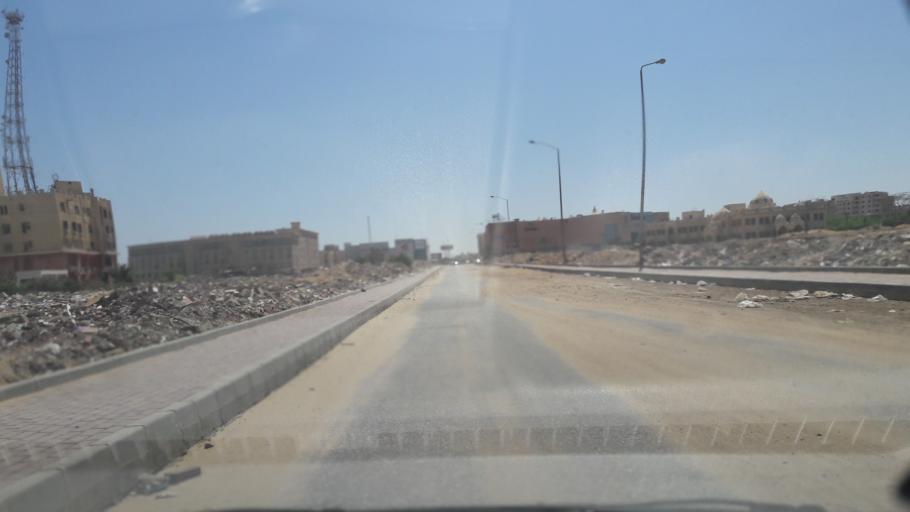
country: EG
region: Al Jizah
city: Madinat Sittah Uktubar
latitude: 29.9646
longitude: 30.9308
